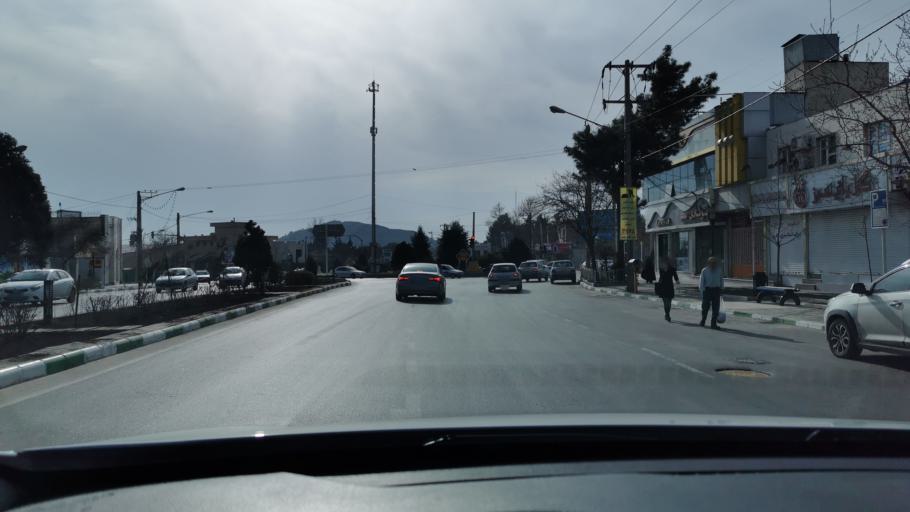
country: IR
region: Razavi Khorasan
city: Mashhad
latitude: 36.2848
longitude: 59.5480
